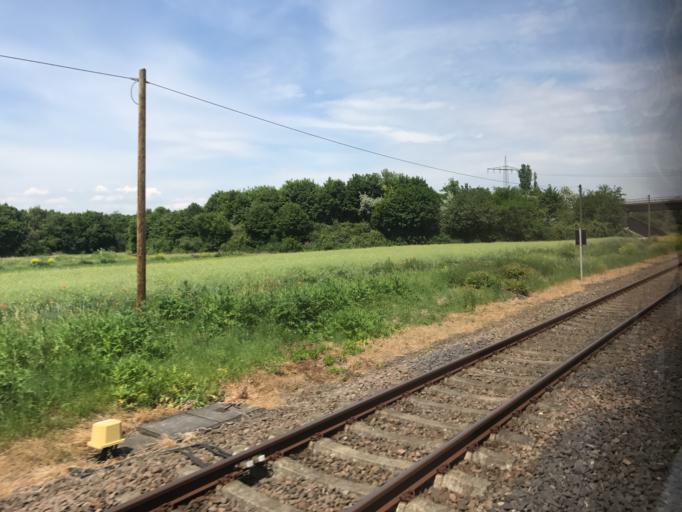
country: DE
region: Rheinland-Pfalz
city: Ockenheim
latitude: 49.9324
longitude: 7.9448
